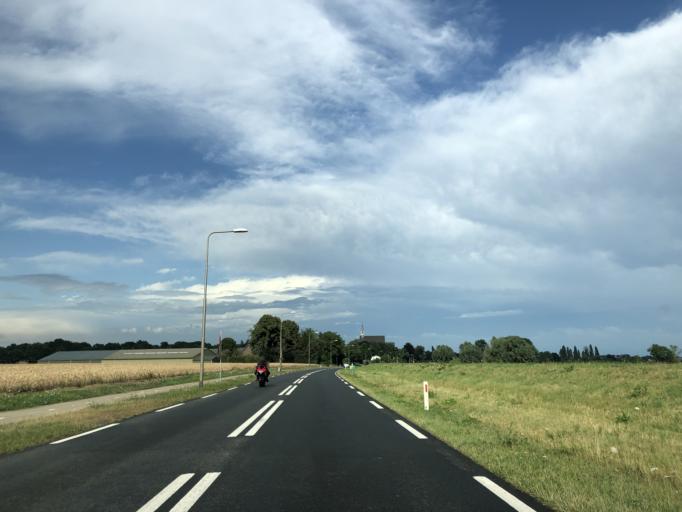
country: NL
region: Limburg
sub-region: Gemeente Gennep
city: Gennep
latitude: 51.7047
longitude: 5.9937
